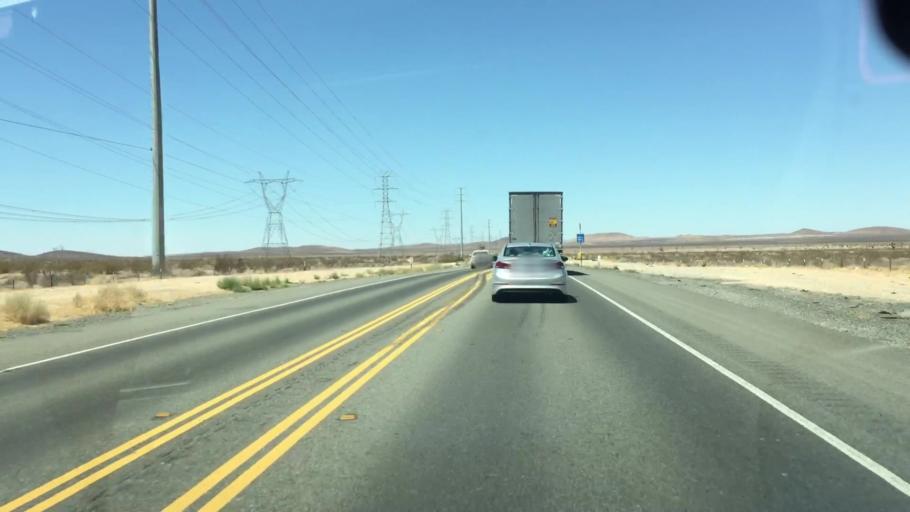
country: US
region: California
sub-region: San Bernardino County
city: Adelanto
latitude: 34.7980
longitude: -117.4866
